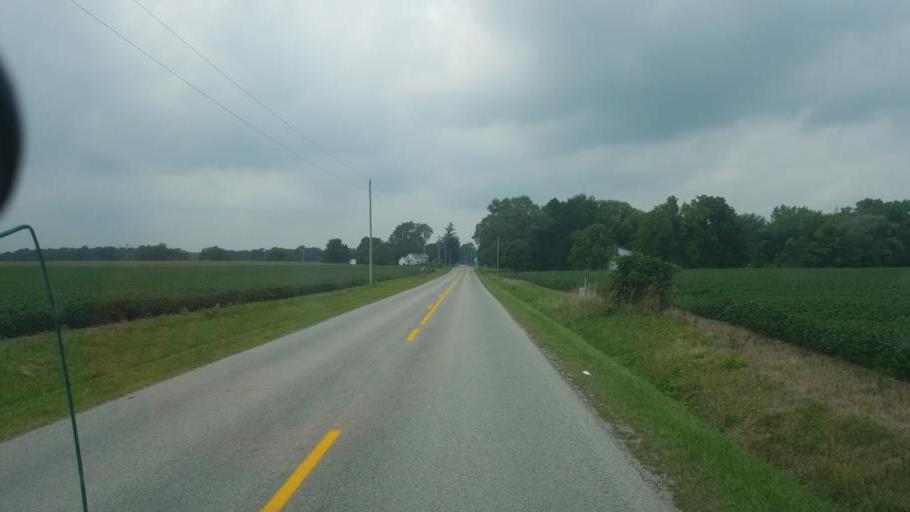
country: US
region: Ohio
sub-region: Huron County
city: Greenwich
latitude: 41.0790
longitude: -82.5594
